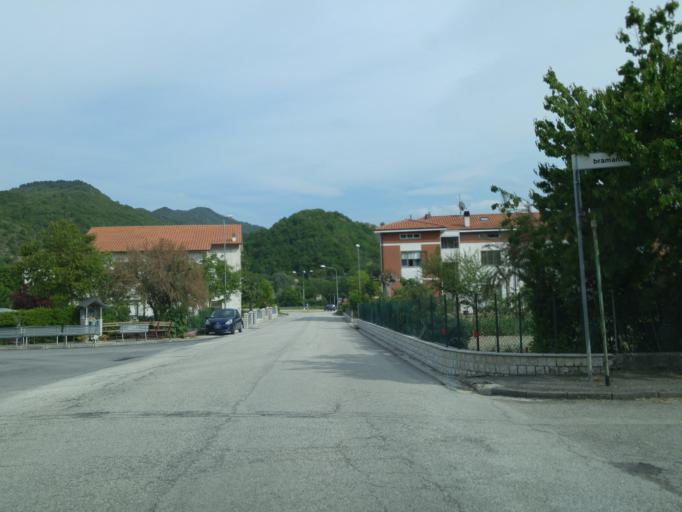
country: IT
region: The Marches
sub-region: Provincia di Pesaro e Urbino
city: Acqualagna
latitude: 43.6264
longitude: 12.6785
